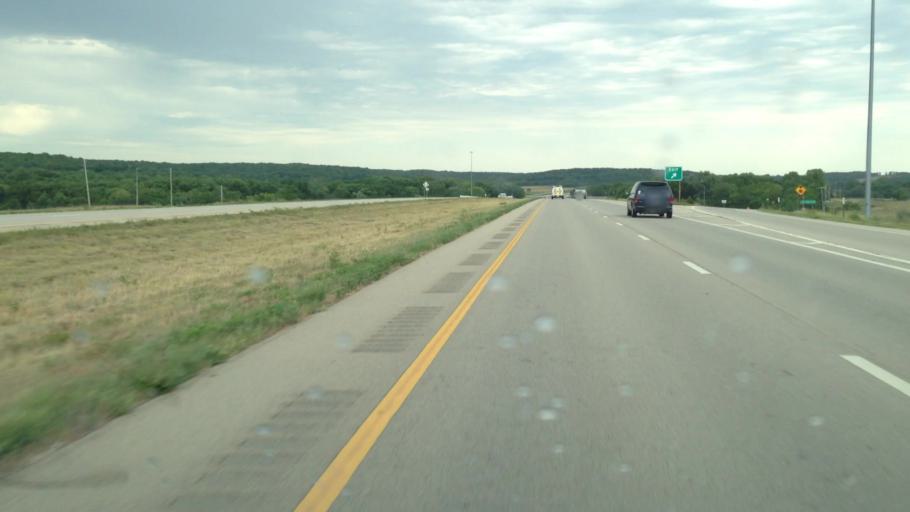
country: US
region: Kansas
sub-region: Douglas County
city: Lawrence
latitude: 38.8875
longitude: -95.2593
